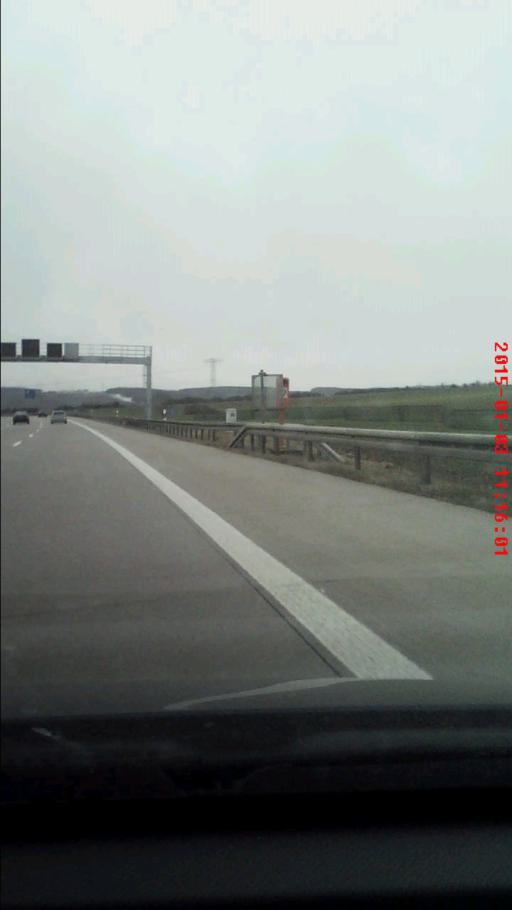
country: DE
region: Thuringia
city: Magdala
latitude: 50.9076
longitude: 11.4199
